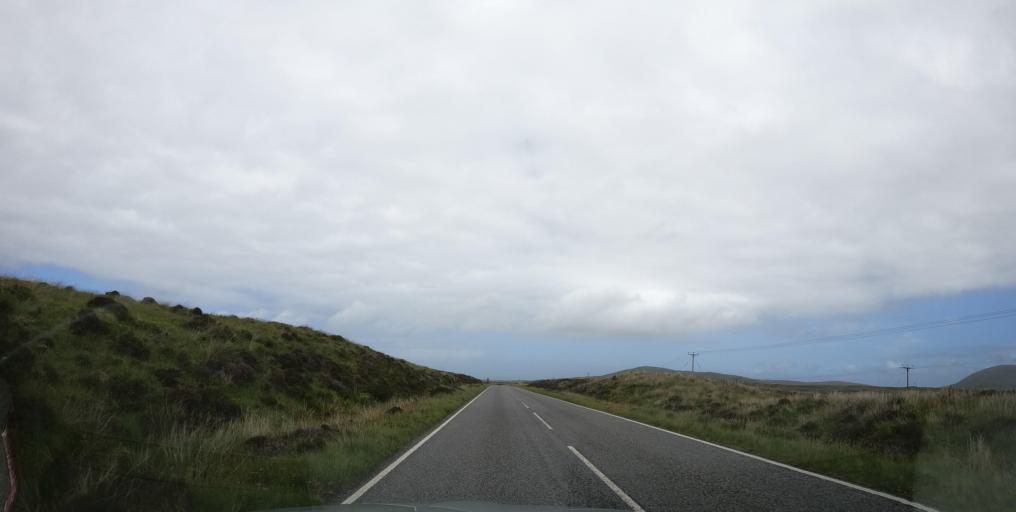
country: GB
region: Scotland
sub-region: Eilean Siar
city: Isle of South Uist
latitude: 57.2743
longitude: -7.3655
